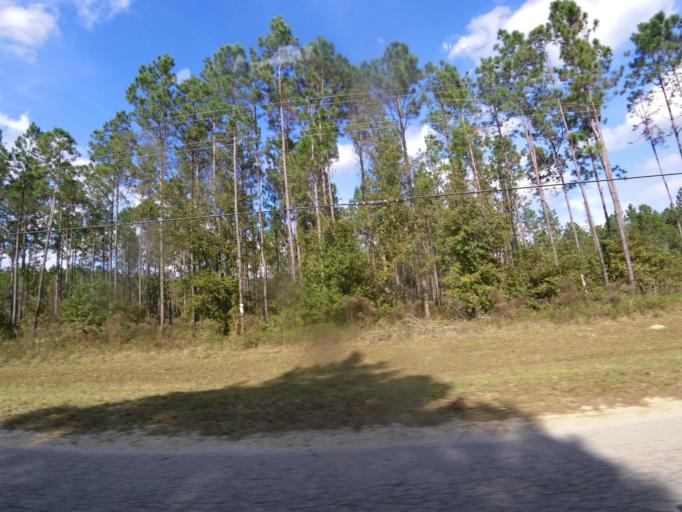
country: US
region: Florida
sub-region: Duval County
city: Baldwin
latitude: 30.1578
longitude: -81.9909
